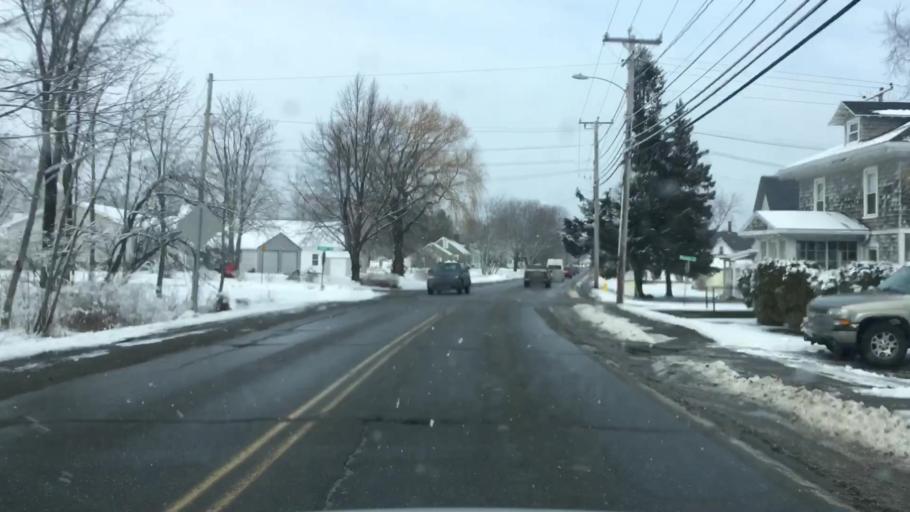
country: US
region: Maine
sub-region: Knox County
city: Rockland
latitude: 44.0924
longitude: -69.1105
